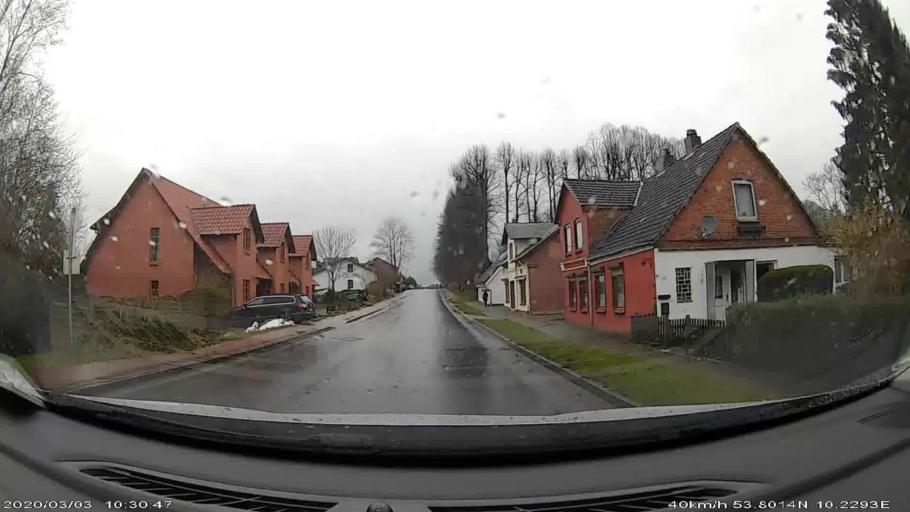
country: DE
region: Schleswig-Holstein
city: Sulfeld
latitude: 53.8026
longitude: 10.2257
